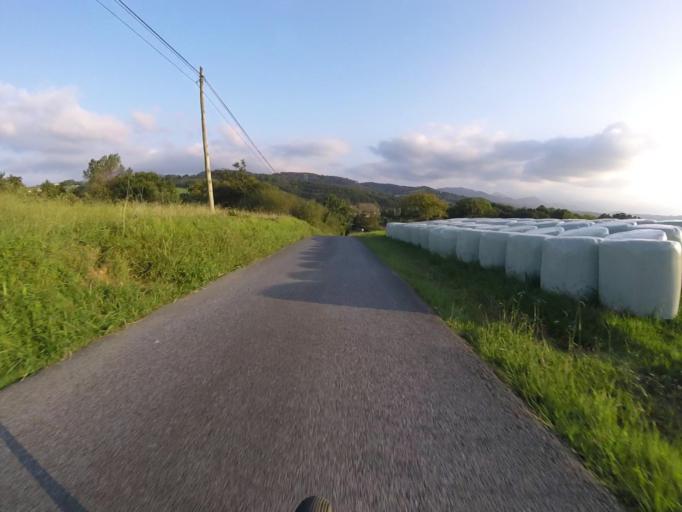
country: ES
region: Basque Country
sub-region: Provincia de Guipuzcoa
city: Lezo
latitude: 43.3295
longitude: -1.8623
